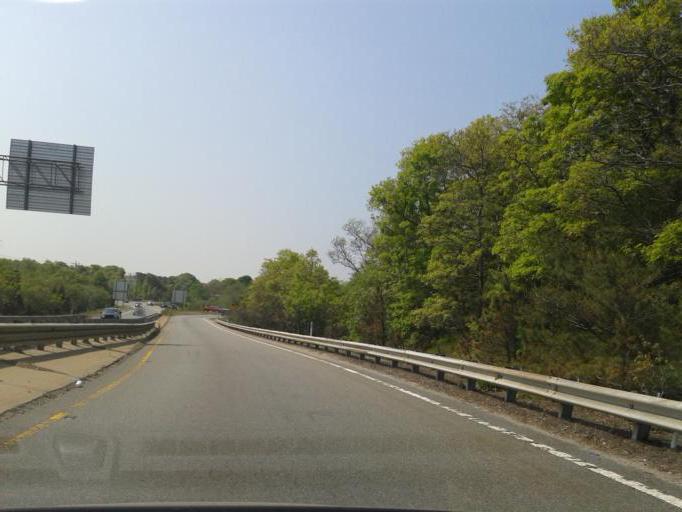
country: US
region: Massachusetts
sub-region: Barnstable County
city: Bourne
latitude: 41.7545
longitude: -70.5967
